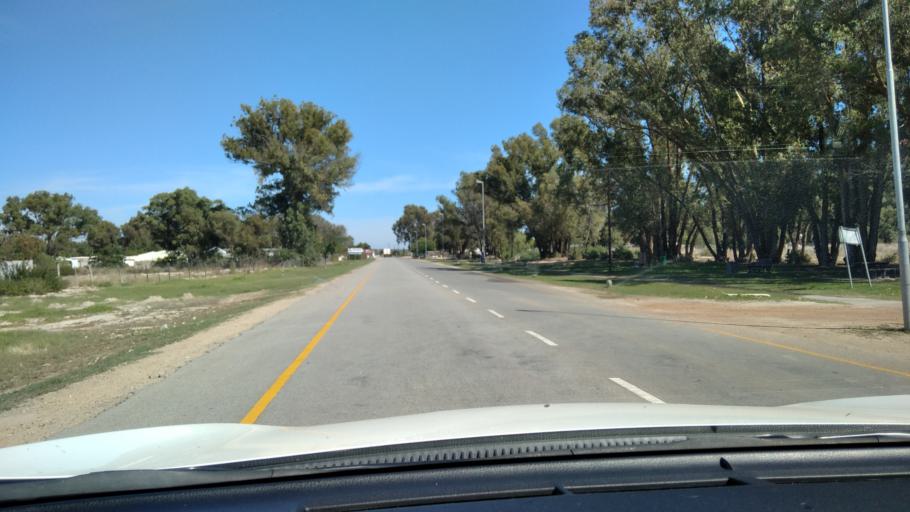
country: ZA
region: Western Cape
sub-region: West Coast District Municipality
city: Moorreesburg
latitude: -33.0570
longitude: 18.3429
